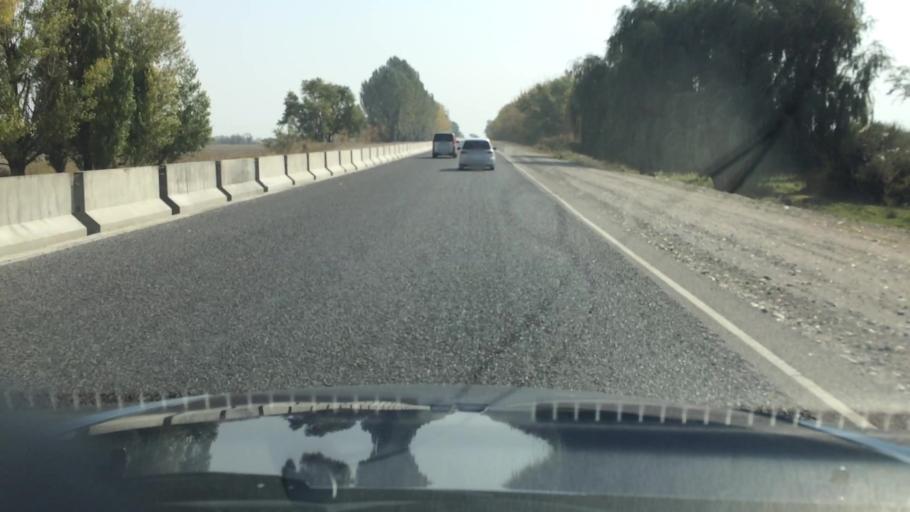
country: KG
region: Chuy
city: Kant
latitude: 42.9656
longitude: 74.9121
